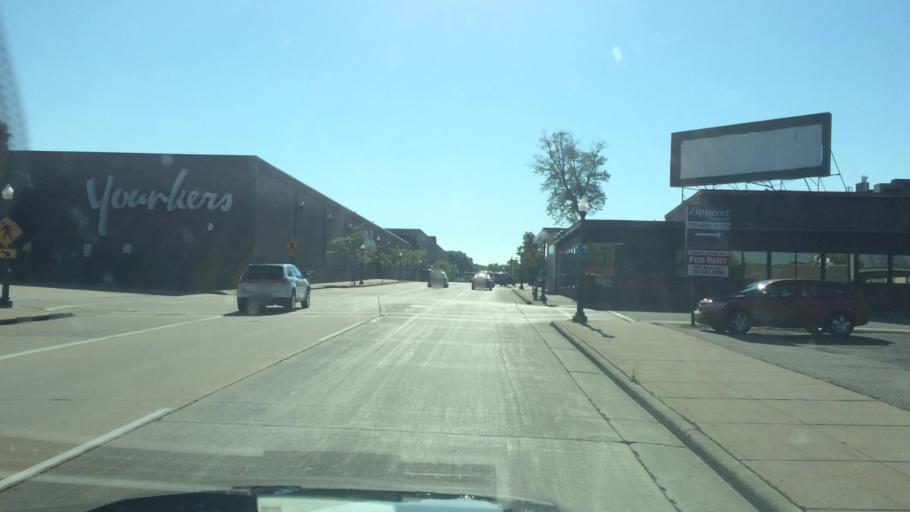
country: US
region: Wisconsin
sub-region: Marathon County
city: Wausau
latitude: 44.9573
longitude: -89.6299
